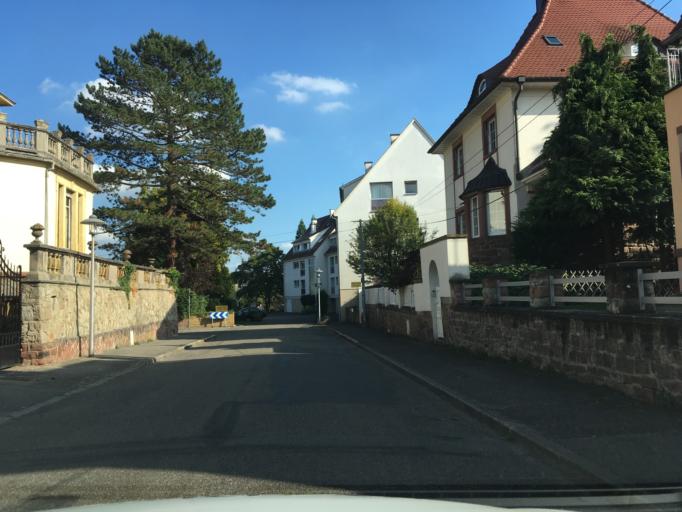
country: FR
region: Alsace
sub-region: Departement du Haut-Rhin
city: Colmar
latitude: 48.0676
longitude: 7.3537
